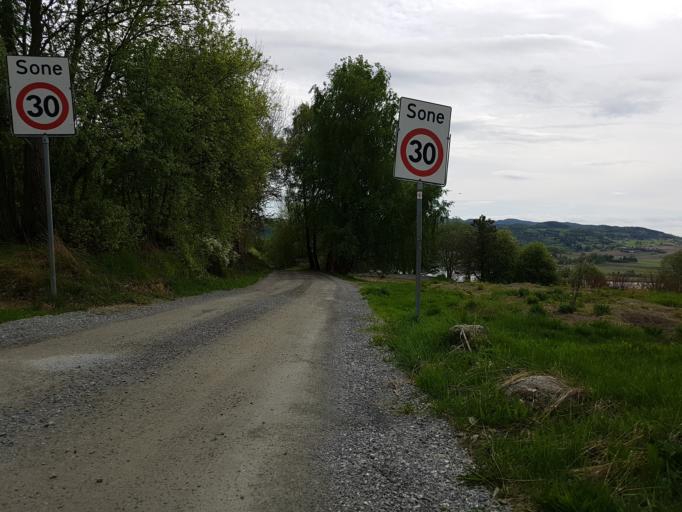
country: NO
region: Nord-Trondelag
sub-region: Levanger
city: Levanger
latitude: 63.7401
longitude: 11.2543
